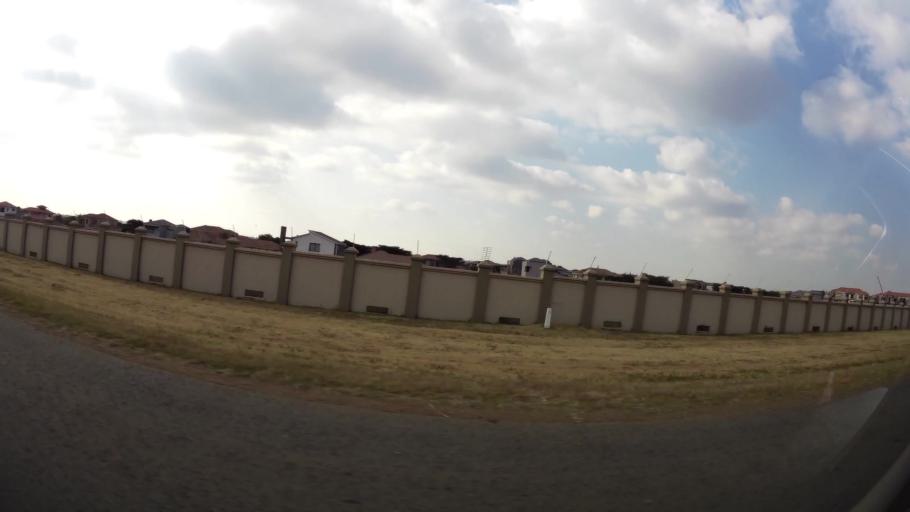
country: ZA
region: Gauteng
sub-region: Ekurhuleni Metropolitan Municipality
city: Benoni
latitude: -26.1443
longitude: 28.2691
